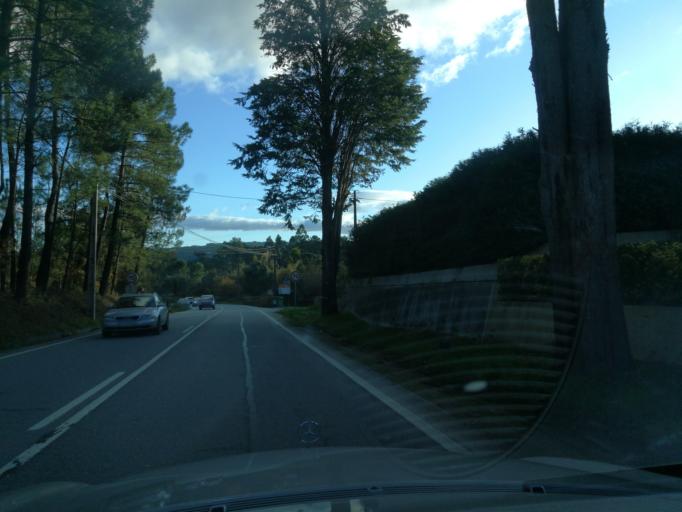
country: PT
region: Braga
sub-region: Esposende
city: Marinhas
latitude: 41.6183
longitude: -8.7554
